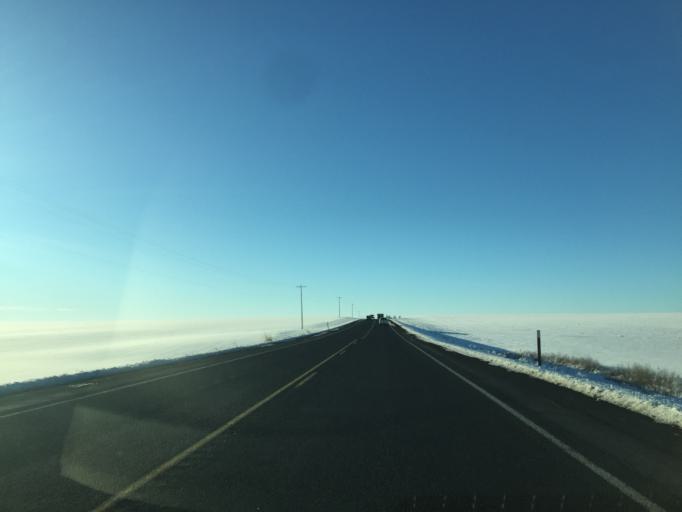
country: US
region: Washington
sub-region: Okanogan County
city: Coulee Dam
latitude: 47.6845
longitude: -119.0004
